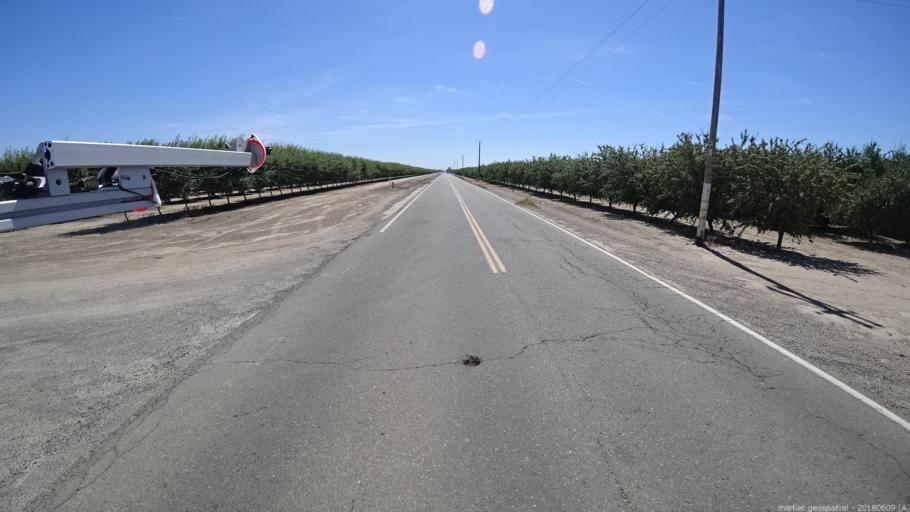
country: US
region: California
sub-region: Madera County
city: Fairmead
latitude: 36.9527
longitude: -120.2201
